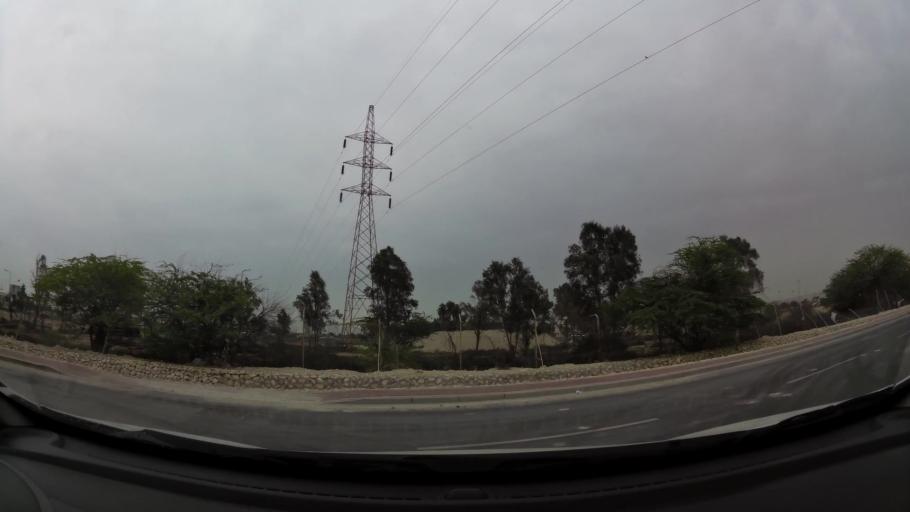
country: BH
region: Northern
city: Madinat `Isa
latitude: 26.1639
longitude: 50.5405
